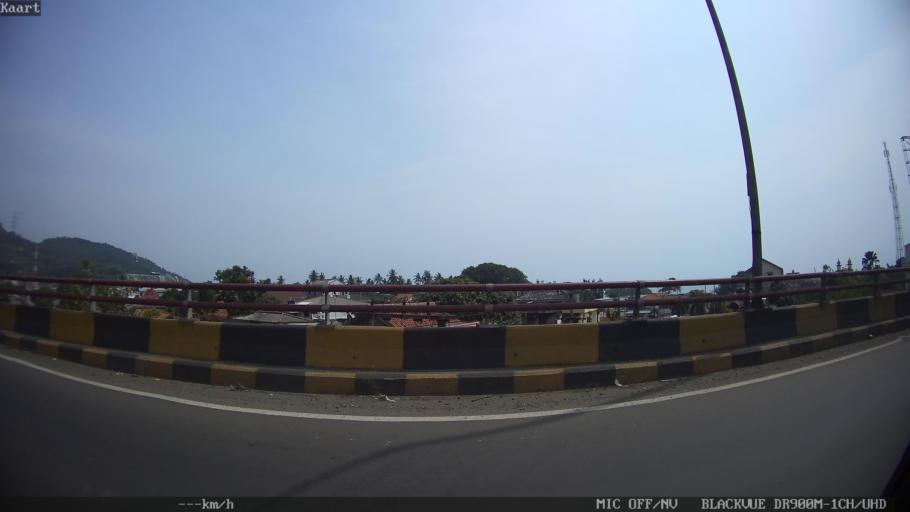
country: ID
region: Banten
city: Curug
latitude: -5.9389
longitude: 106.0019
